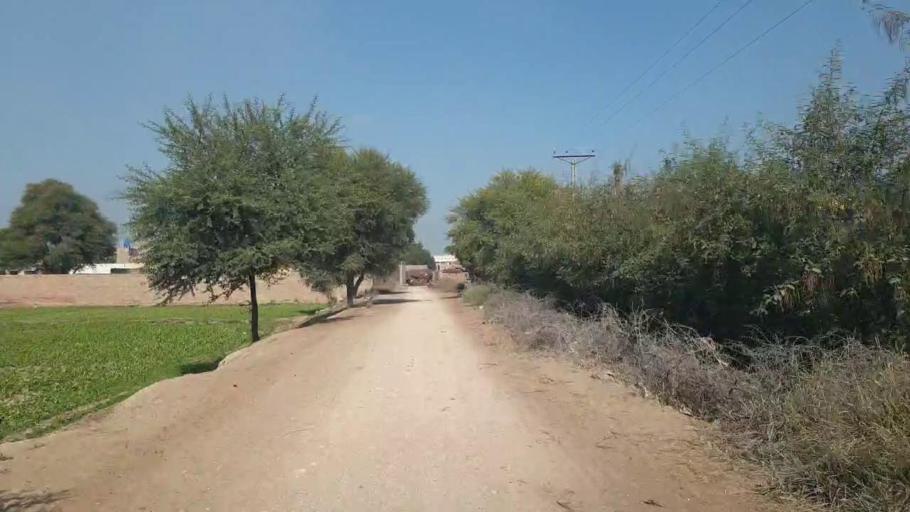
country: PK
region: Sindh
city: Shahdadpur
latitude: 25.9309
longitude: 68.5859
